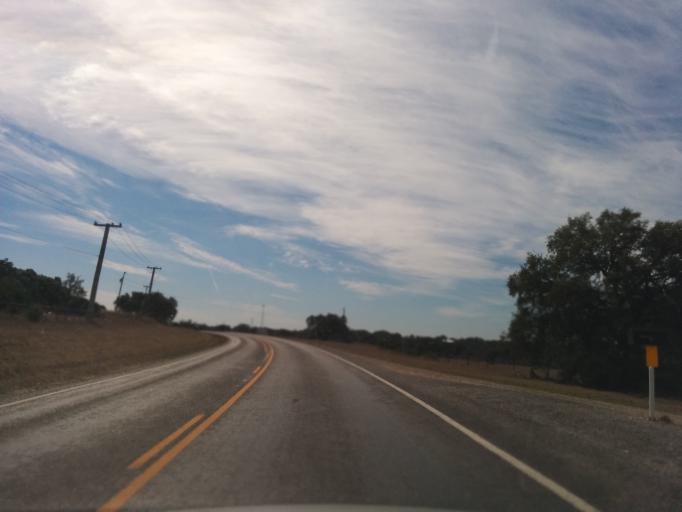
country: US
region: Texas
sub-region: Bexar County
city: Fair Oaks Ranch
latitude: 29.8781
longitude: -98.5589
